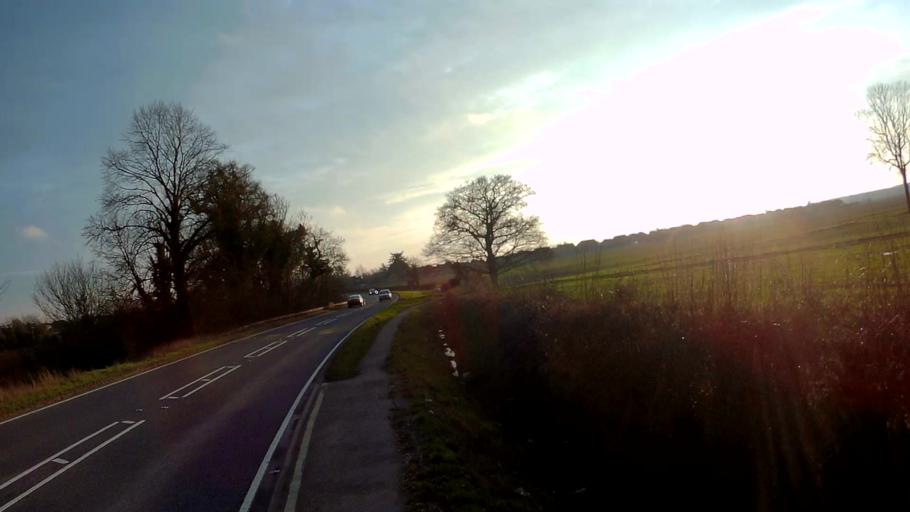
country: GB
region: England
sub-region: Lincolnshire
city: Bourne
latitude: 52.7820
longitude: -0.3769
